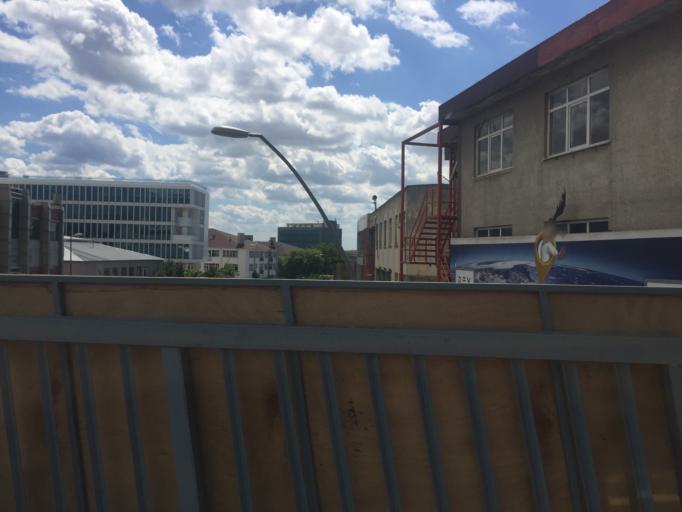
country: TR
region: Istanbul
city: merter keresteciler
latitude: 41.0307
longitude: 28.9149
